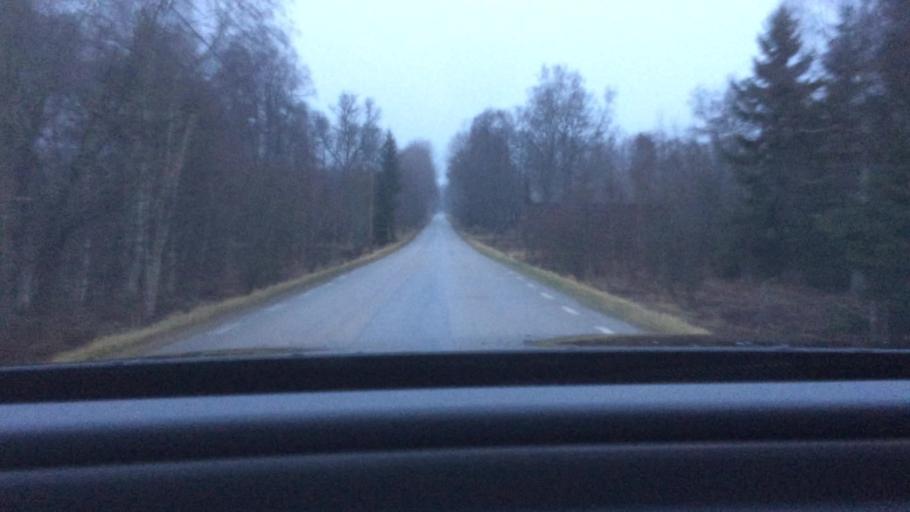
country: SE
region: Vaestra Goetaland
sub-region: Ulricehamns Kommun
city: Ulricehamn
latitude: 57.9592
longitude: 13.3955
